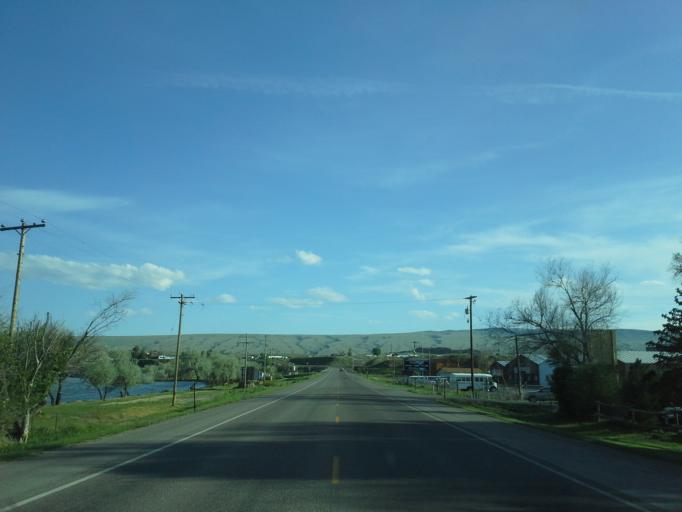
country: US
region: Wyoming
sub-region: Hot Springs County
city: Thermopolis
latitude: 43.6240
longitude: -108.2208
